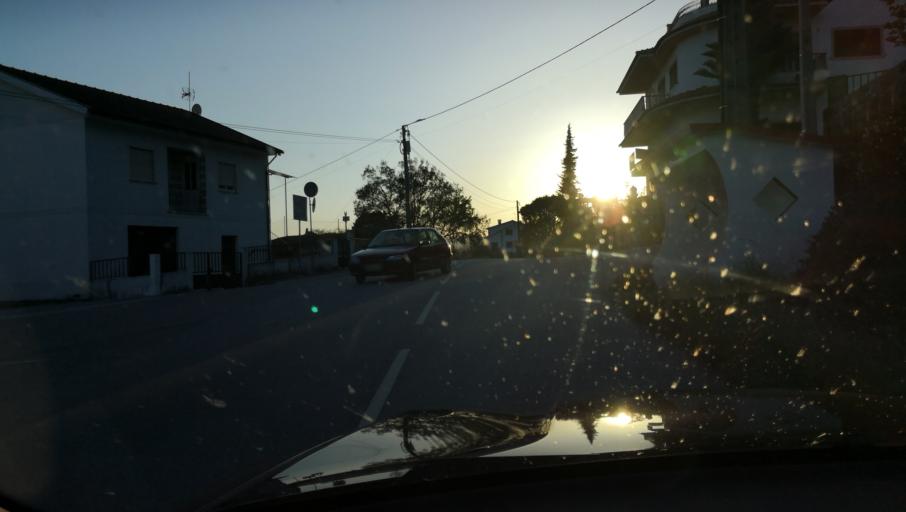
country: PT
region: Vila Real
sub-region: Mondim de Basto
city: Mondim de Basto
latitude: 41.4068
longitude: -7.9223
